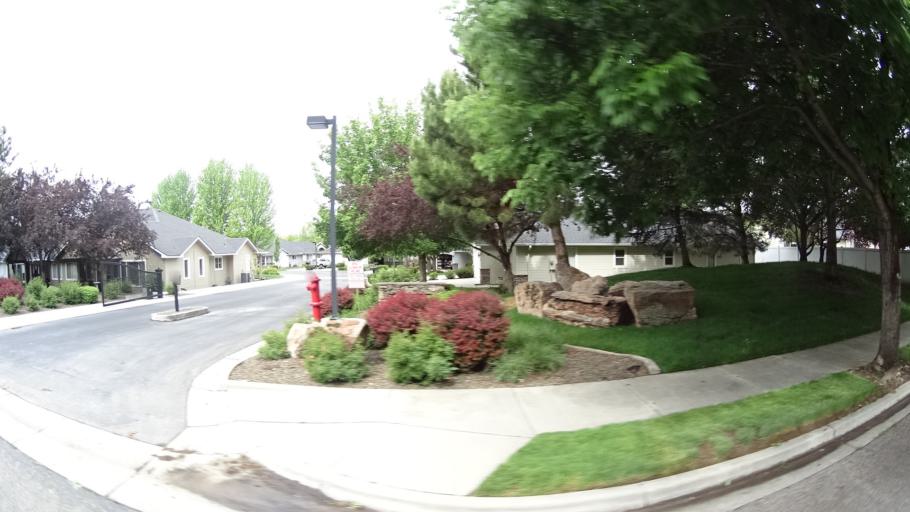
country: US
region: Idaho
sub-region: Ada County
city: Eagle
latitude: 43.7033
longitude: -116.3540
